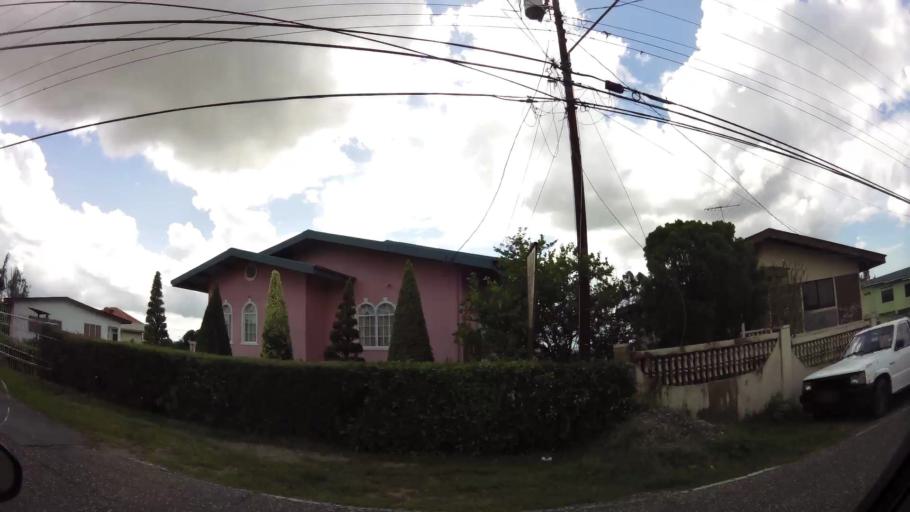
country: TT
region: Penal/Debe
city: Debe
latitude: 10.2288
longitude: -61.4404
